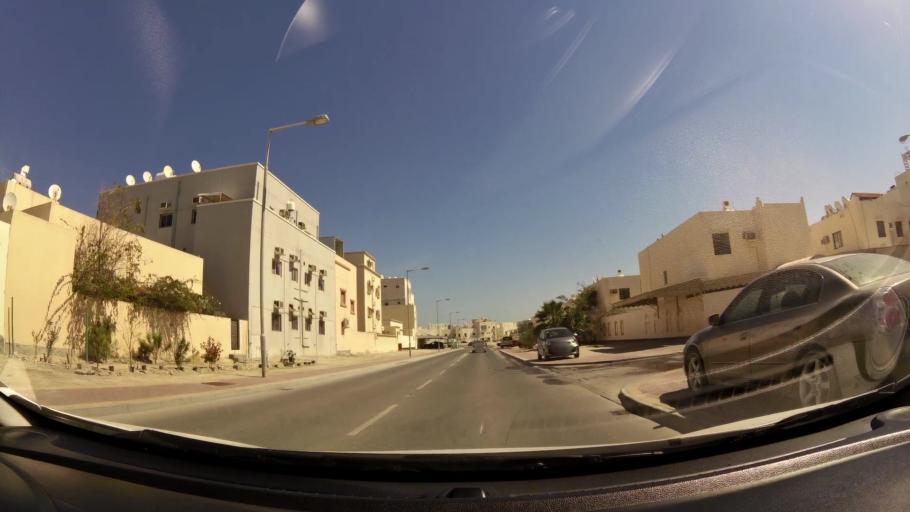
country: BH
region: Muharraq
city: Al Hadd
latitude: 26.2736
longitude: 50.6554
